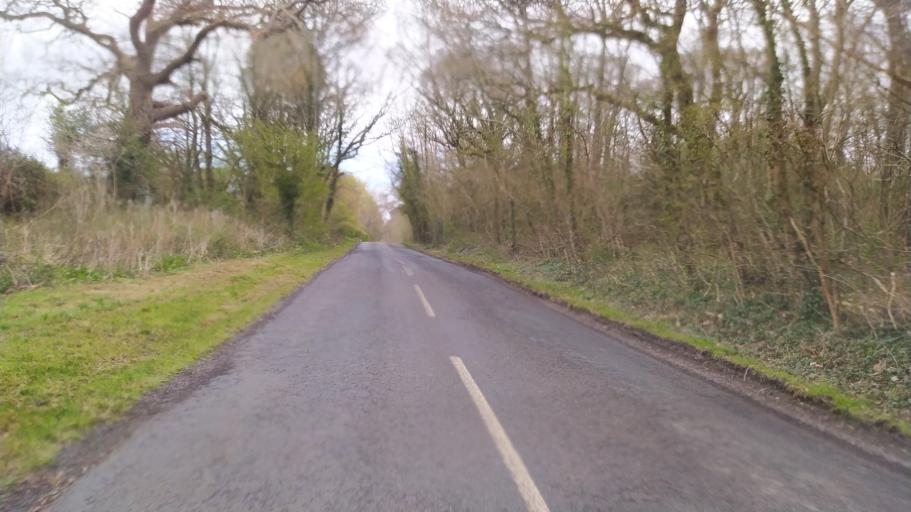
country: GB
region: England
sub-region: West Sussex
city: Petworth
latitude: 51.0183
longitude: -0.6042
